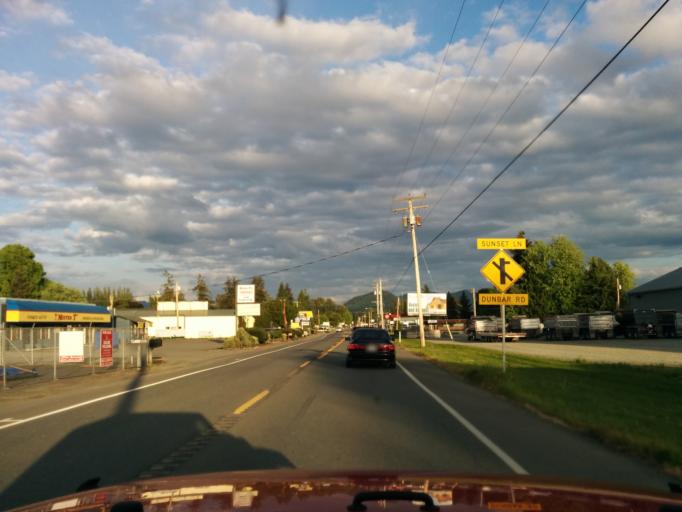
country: US
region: Washington
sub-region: Skagit County
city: Mount Vernon
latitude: 48.4291
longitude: -122.3647
